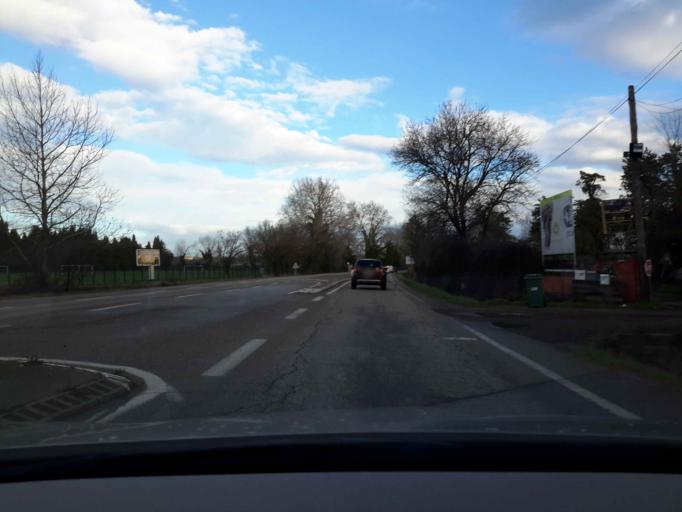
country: FR
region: Languedoc-Roussillon
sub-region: Departement du Gard
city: Caissargues
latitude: 43.7889
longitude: 4.3516
